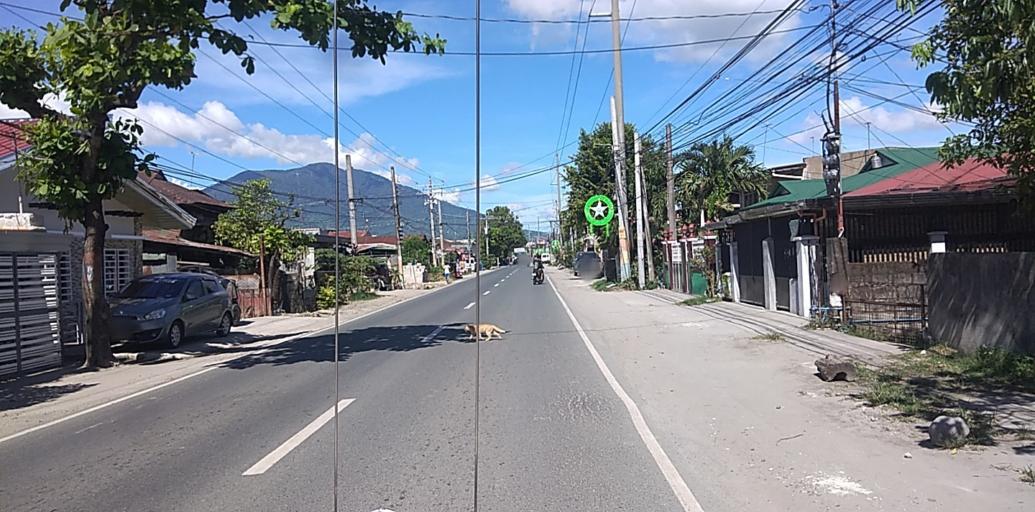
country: PH
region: Central Luzon
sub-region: Province of Pampanga
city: Arayat
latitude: 15.1318
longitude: 120.7747
